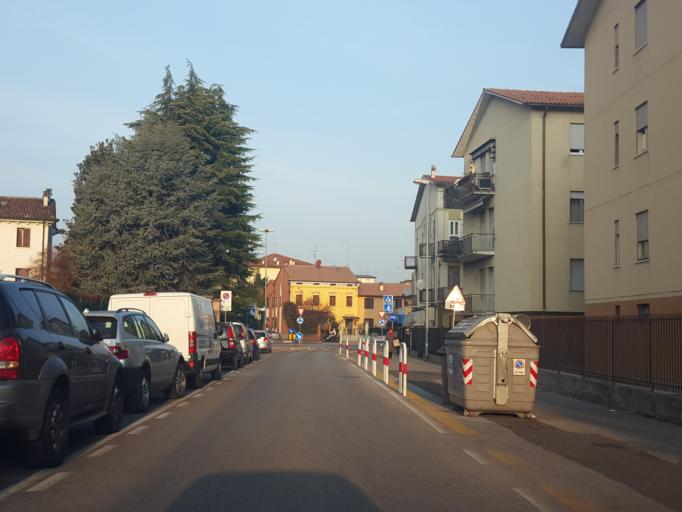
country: IT
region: Veneto
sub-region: Provincia di Vicenza
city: Vicenza
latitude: 45.5619
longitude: 11.5656
